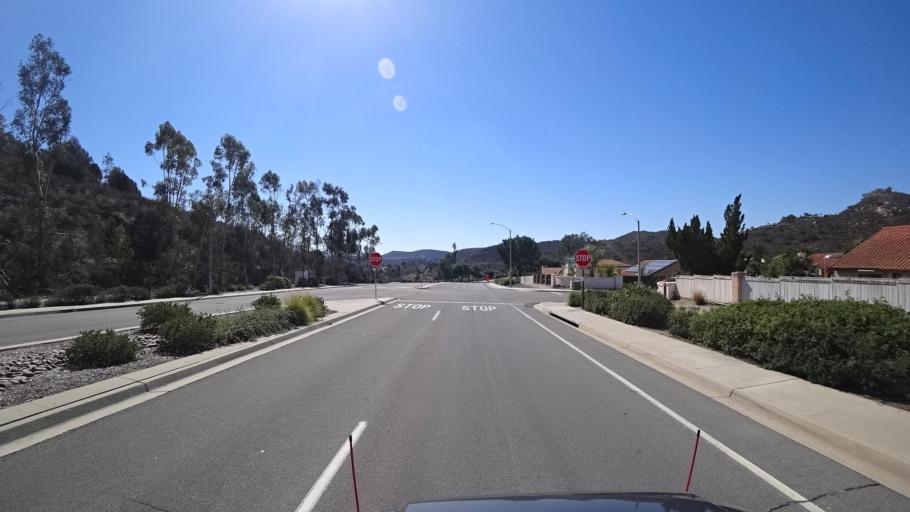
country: US
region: California
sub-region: San Diego County
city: Rancho San Diego
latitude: 32.7537
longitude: -116.9390
